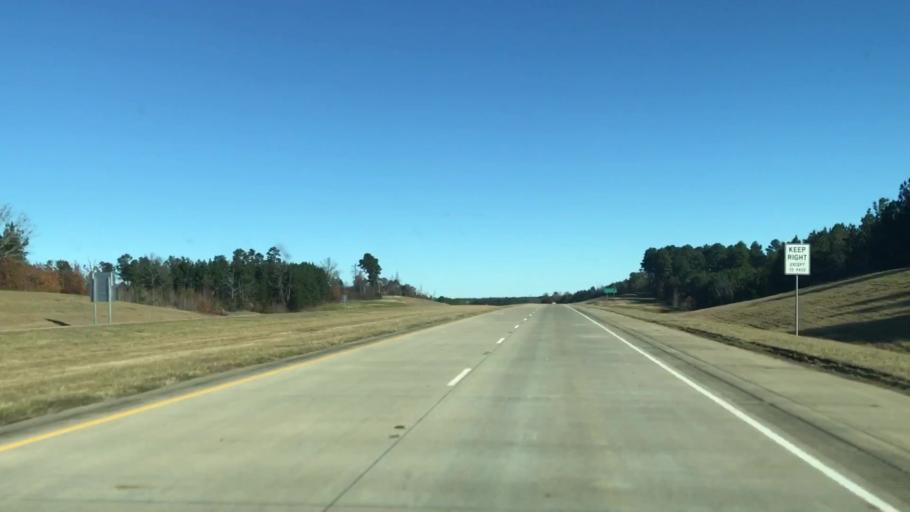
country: US
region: Louisiana
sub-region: Caddo Parish
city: Vivian
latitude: 33.0098
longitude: -93.9042
